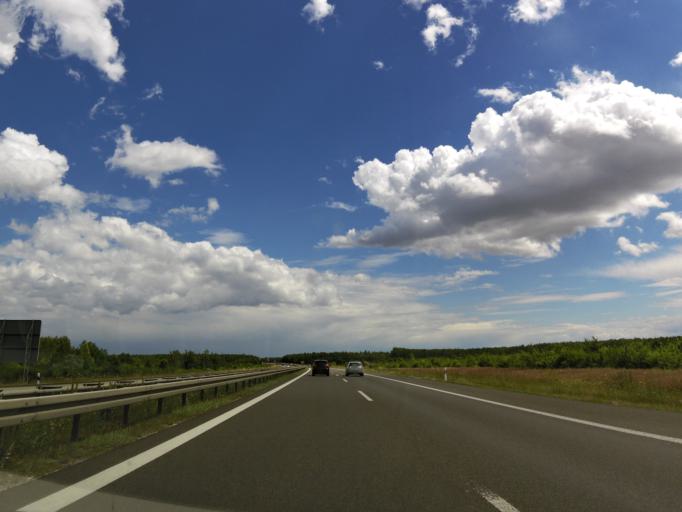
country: DE
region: Saxony
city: Zwenkau
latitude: 51.2478
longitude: 12.3216
